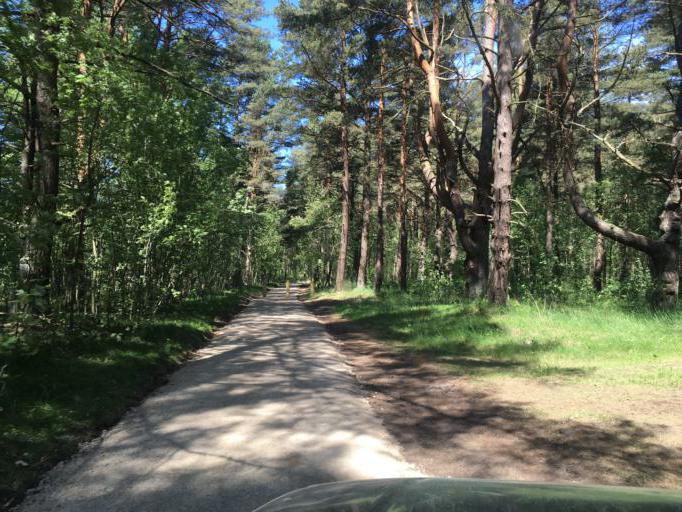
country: LV
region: Ventspils
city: Ventspils
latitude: 57.4590
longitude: 21.6455
